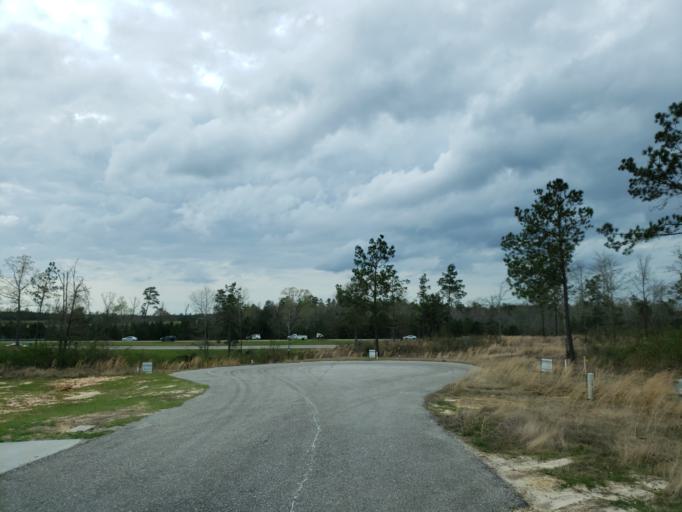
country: US
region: Mississippi
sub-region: Jones County
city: Ellisville
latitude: 31.5543
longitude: -89.2595
